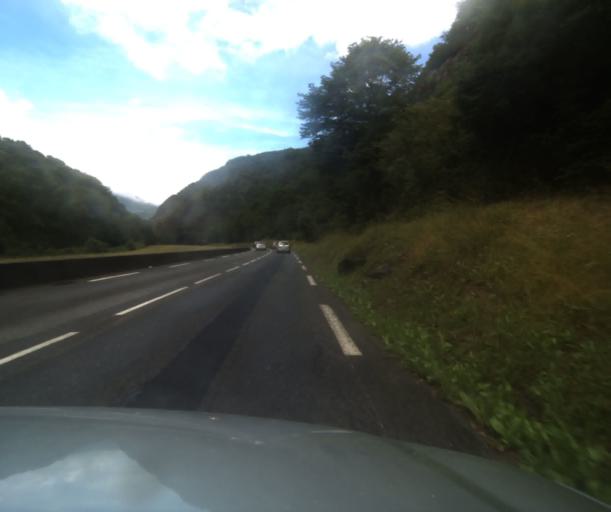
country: FR
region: Midi-Pyrenees
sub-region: Departement des Hautes-Pyrenees
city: Pierrefitte-Nestalas
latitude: 42.9434
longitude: -0.0532
